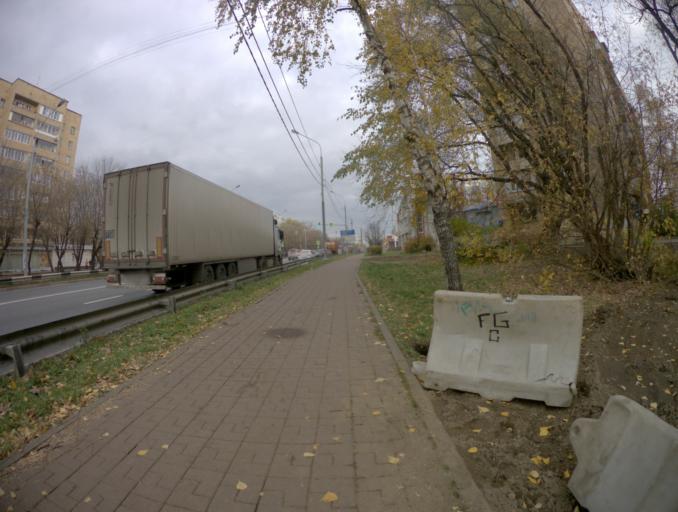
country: RU
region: Moskovskaya
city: Orekhovo-Zuyevo
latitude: 55.8070
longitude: 38.9681
